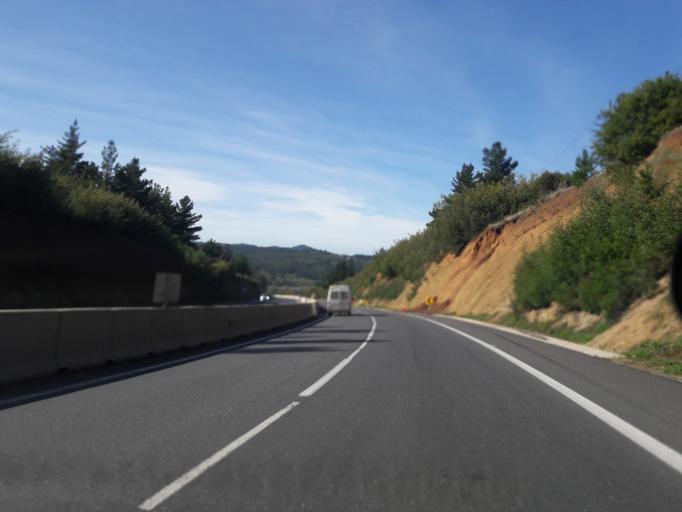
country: CL
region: Biobio
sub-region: Provincia de Biobio
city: Yumbel
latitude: -36.9781
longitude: -72.6494
